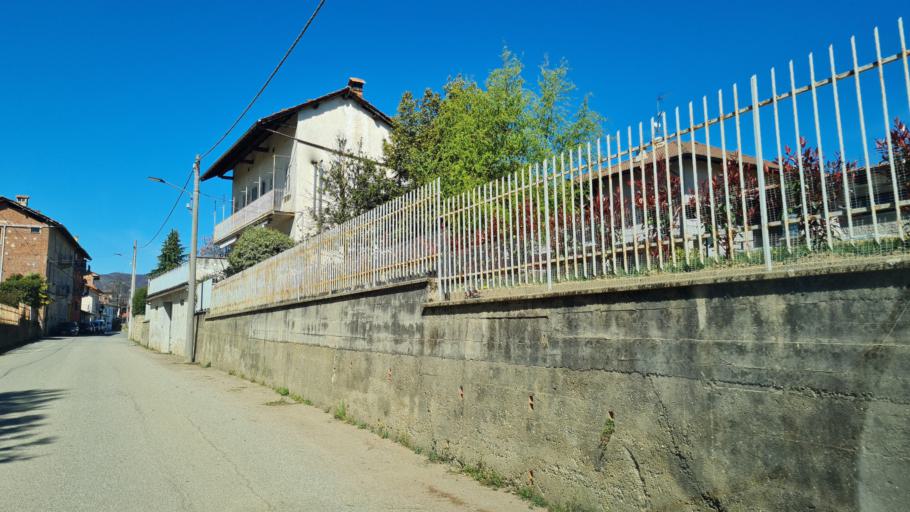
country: IT
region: Piedmont
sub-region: Provincia di Novara
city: Maggiora
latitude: 45.6873
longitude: 8.4322
